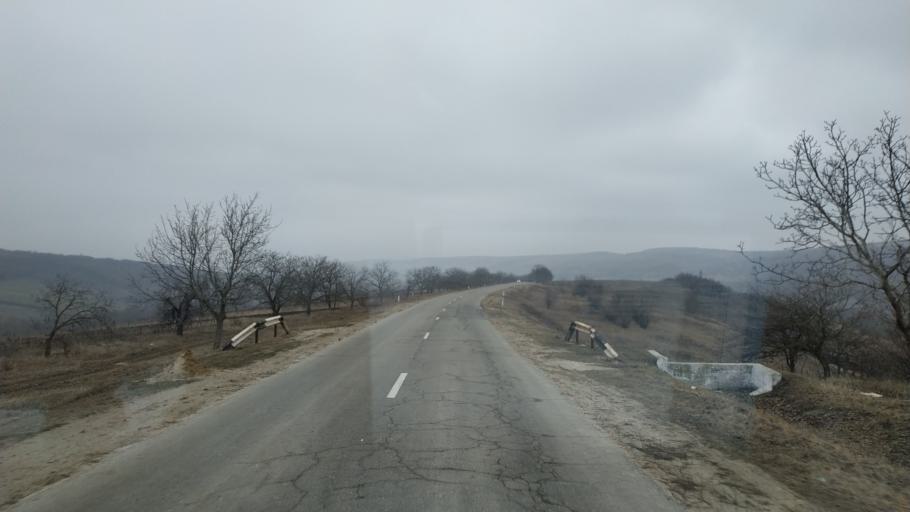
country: MD
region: Stinga Nistrului
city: Bucovat
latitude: 47.0066
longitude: 28.4361
